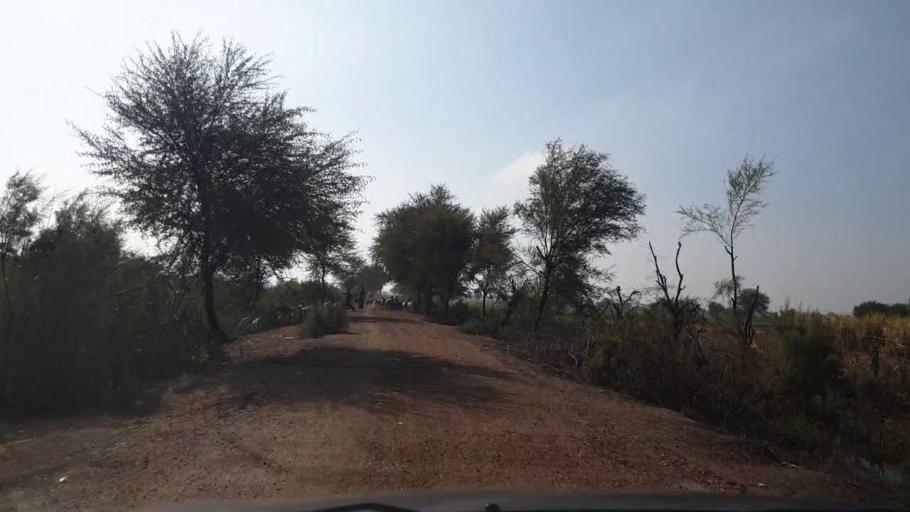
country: PK
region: Sindh
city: Sinjhoro
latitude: 26.0523
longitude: 68.7833
